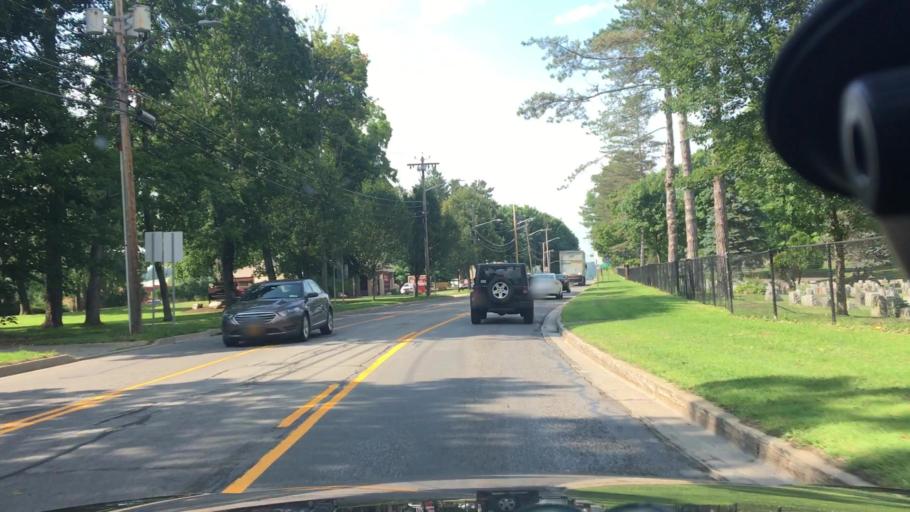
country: US
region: New York
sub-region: Chautauqua County
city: Jamestown
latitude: 42.1155
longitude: -79.2407
